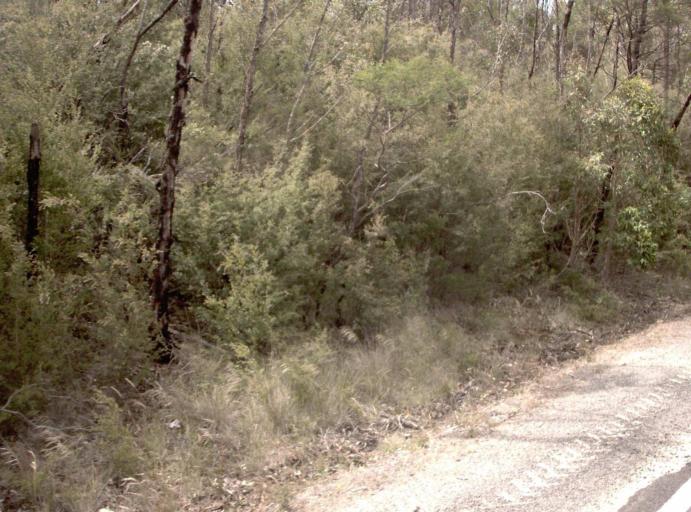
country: AU
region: New South Wales
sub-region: Bega Valley
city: Eden
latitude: -37.4611
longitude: 149.5894
